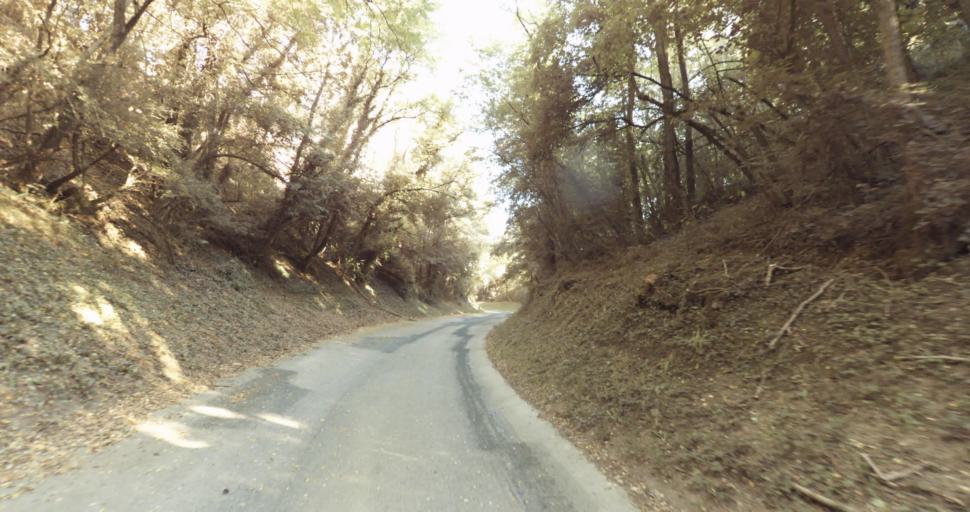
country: FR
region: Rhone-Alpes
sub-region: Departement du Rhone
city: Genay
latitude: 45.8864
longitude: 4.8409
